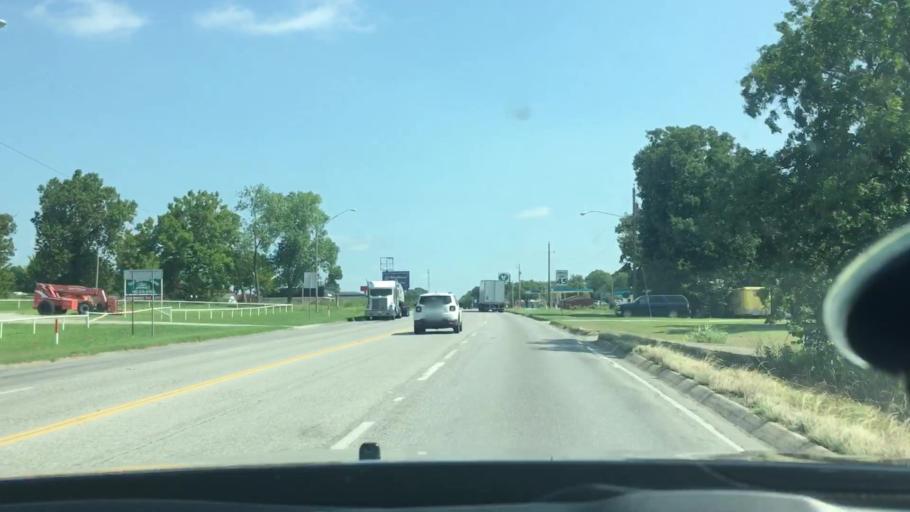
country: US
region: Oklahoma
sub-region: Atoka County
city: Atoka
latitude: 34.3177
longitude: -96.1685
